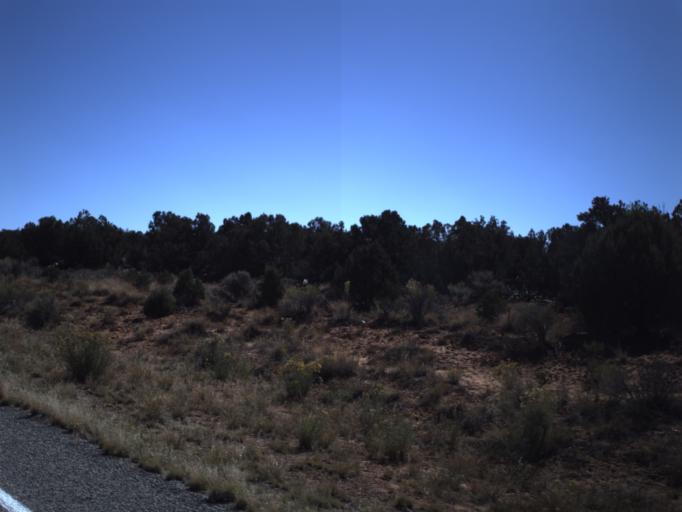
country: US
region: Utah
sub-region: San Juan County
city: Blanding
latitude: 37.5412
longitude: -109.9723
